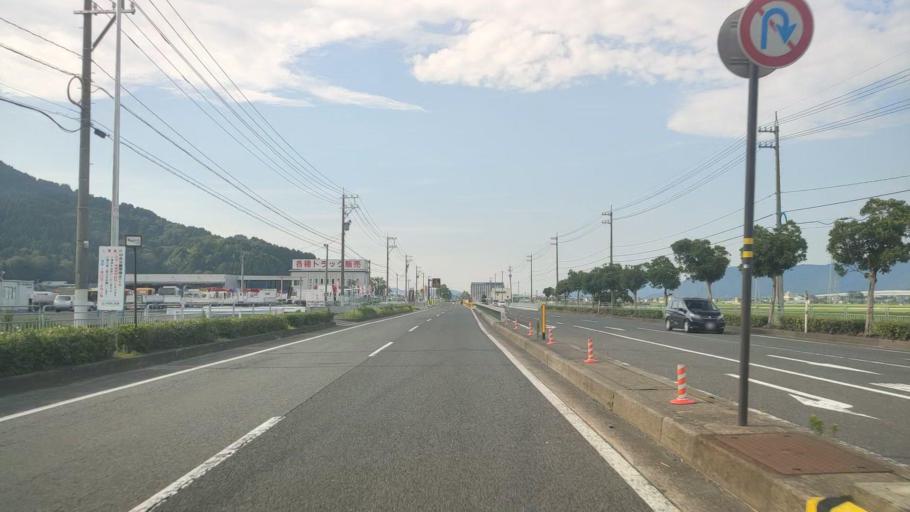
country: JP
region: Fukui
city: Takefu
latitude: 35.8936
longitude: 136.1924
